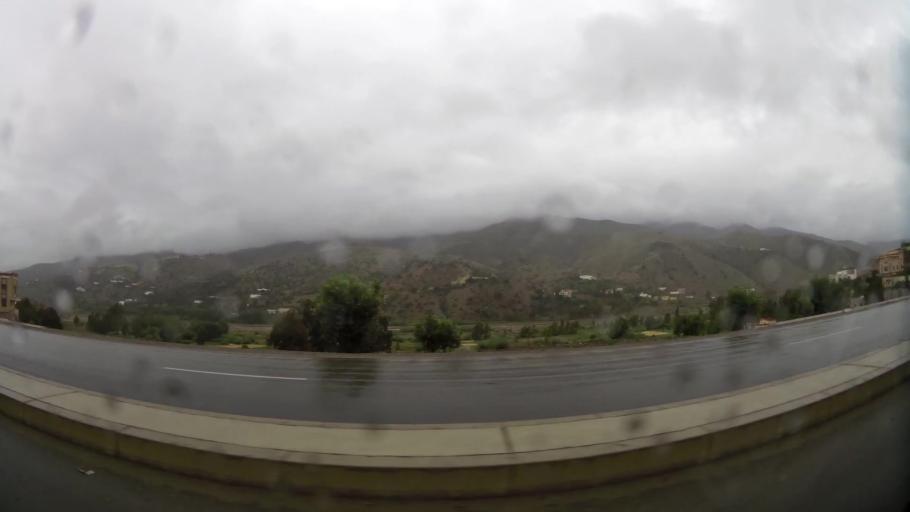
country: MA
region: Taza-Al Hoceima-Taounate
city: Imzourene
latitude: 35.0244
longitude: -3.8225
